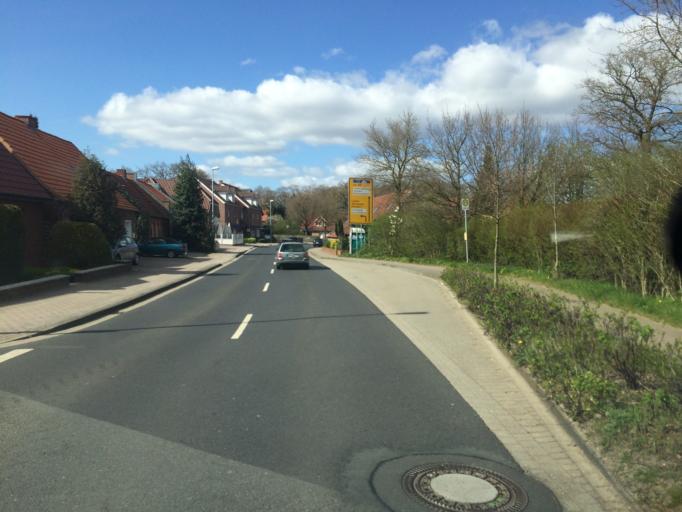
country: DE
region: Lower Saxony
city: Haren
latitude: 52.7879
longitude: 7.2269
